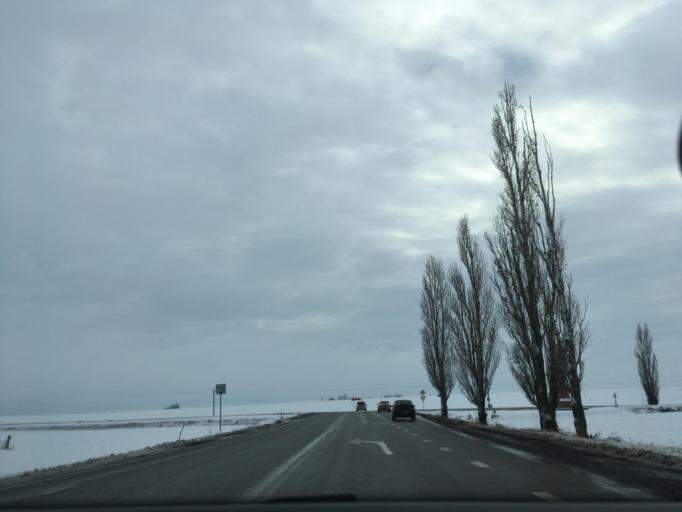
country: UA
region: Luhansk
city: Lozno-Oleksandrivka
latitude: 49.9523
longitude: 38.9547
